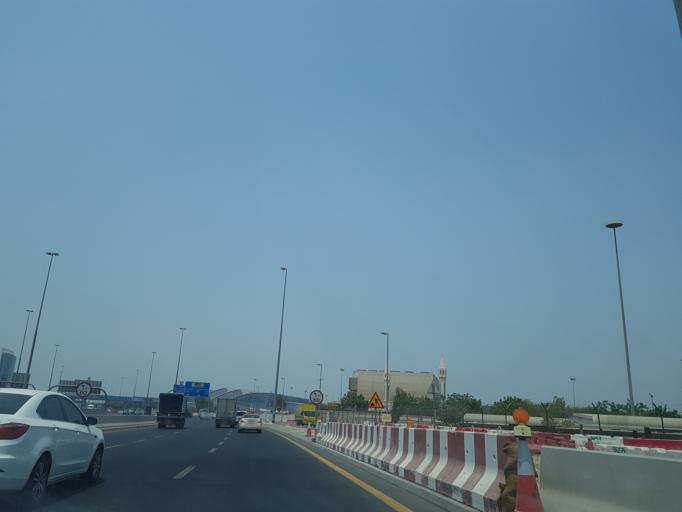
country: AE
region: Ash Shariqah
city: Sharjah
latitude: 25.2567
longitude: 55.3377
